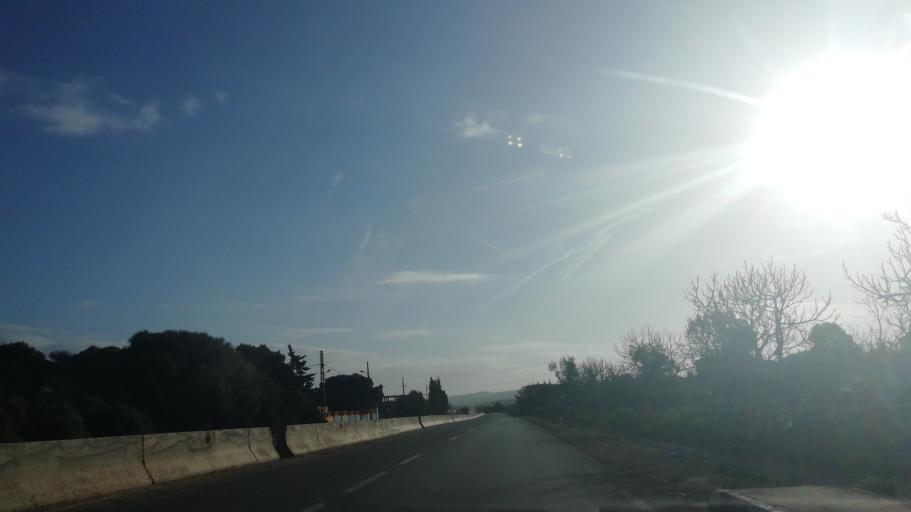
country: DZ
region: Mostaganem
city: Mostaganem
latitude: 36.1069
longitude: 0.3023
